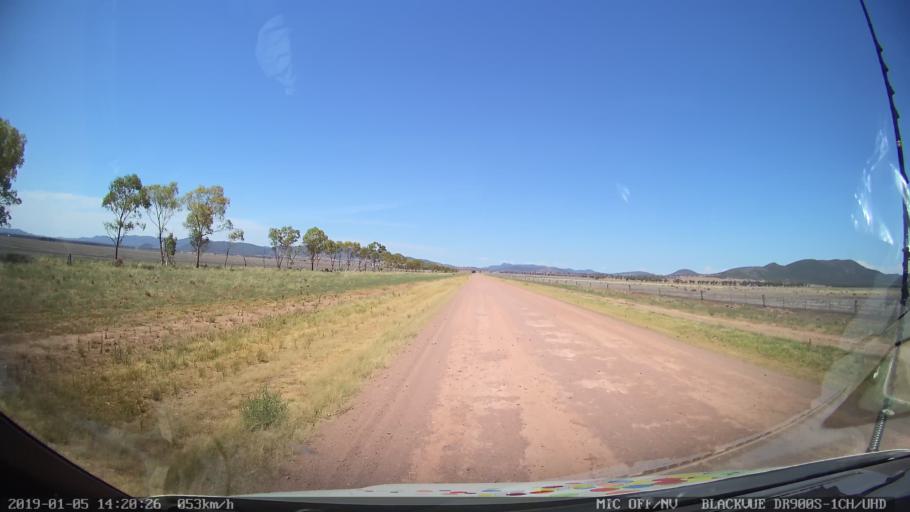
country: AU
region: New South Wales
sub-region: Liverpool Plains
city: Quirindi
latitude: -31.2487
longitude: 150.5047
